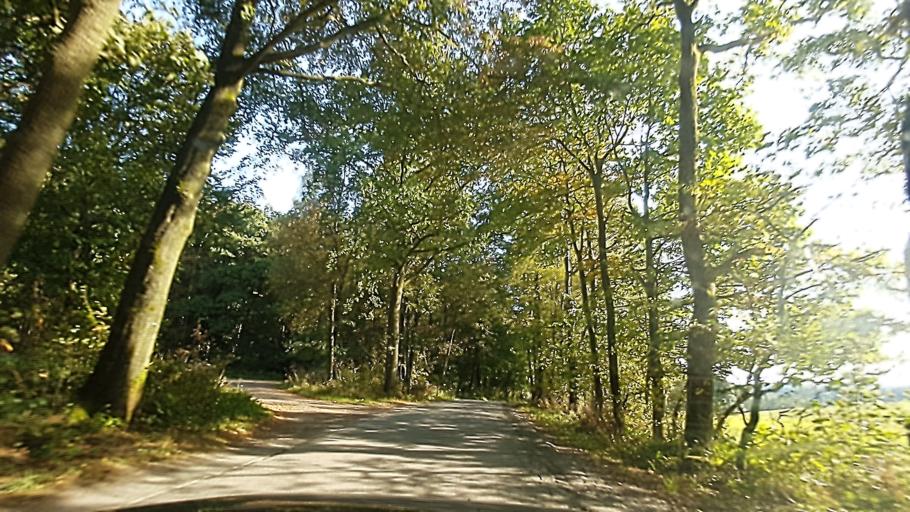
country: DE
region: North Rhine-Westphalia
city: Halver
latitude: 51.1400
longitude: 7.4843
